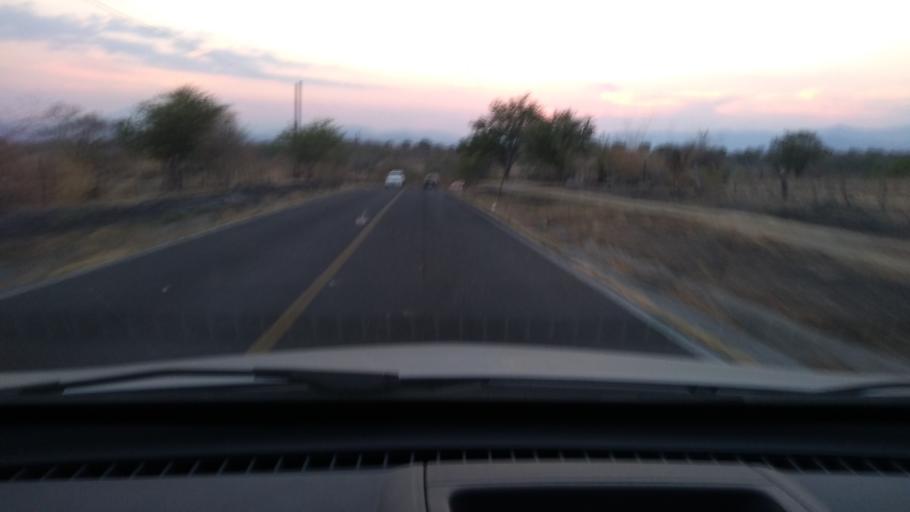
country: MX
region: Morelos
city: Coatetelco
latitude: 18.7231
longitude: -99.2931
